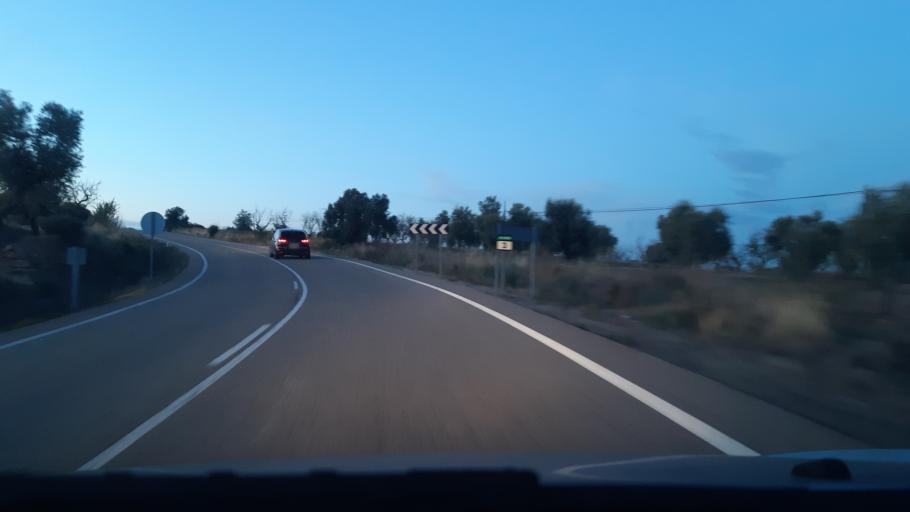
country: ES
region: Aragon
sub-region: Provincia de Teruel
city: Calaceite
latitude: 40.9898
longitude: 0.1991
